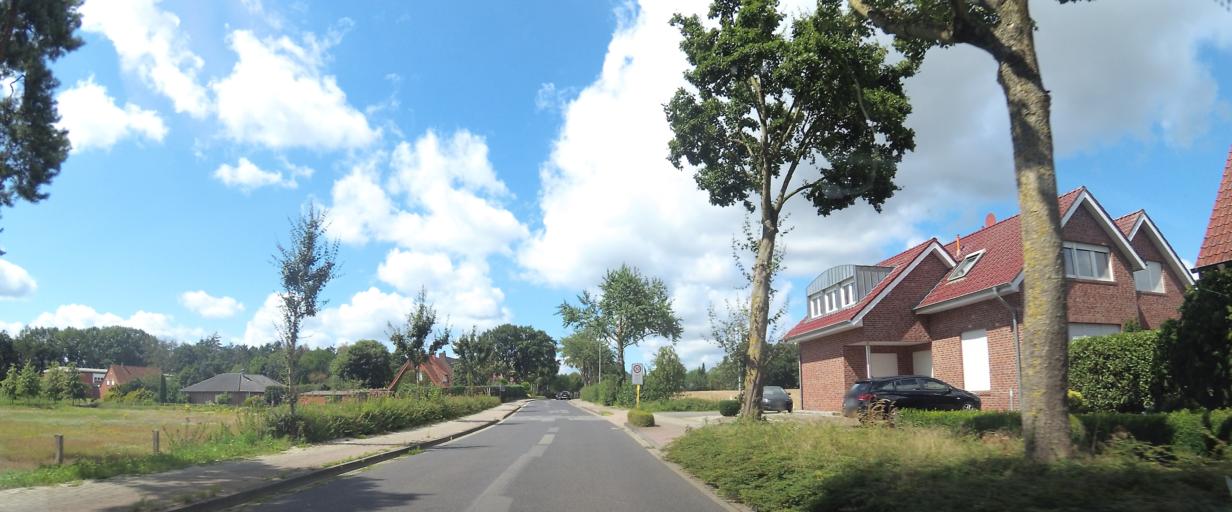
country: DE
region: Lower Saxony
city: Haren
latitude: 52.7887
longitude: 7.2840
